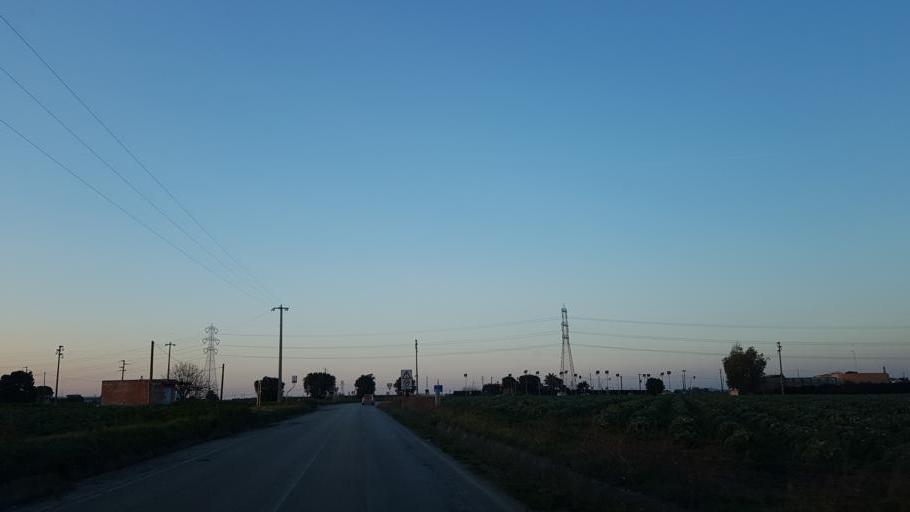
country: IT
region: Apulia
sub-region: Provincia di Brindisi
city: La Rosa
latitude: 40.5886
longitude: 17.9445
